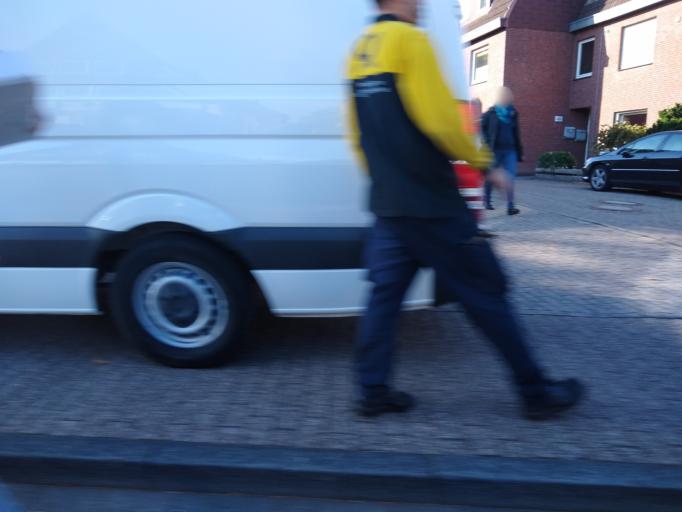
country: DE
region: Lower Saxony
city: Oldenburg
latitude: 53.1847
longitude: 8.2034
